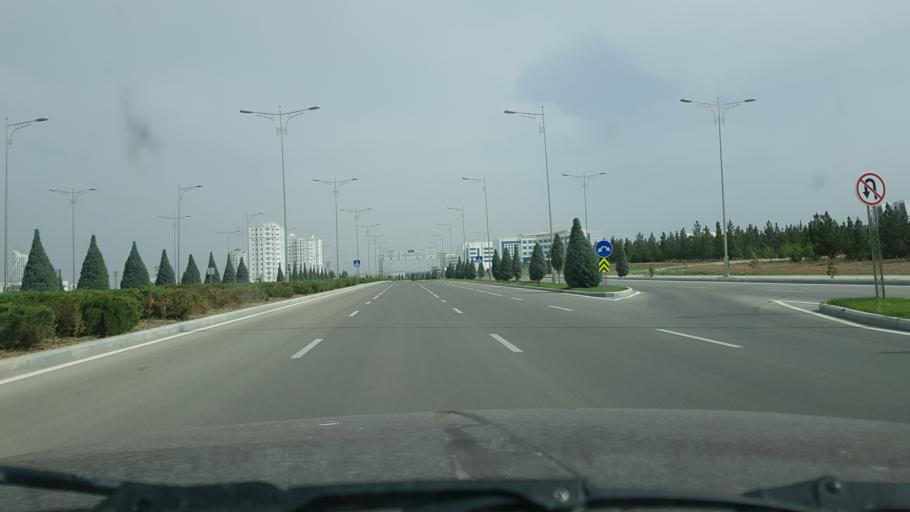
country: TM
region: Ahal
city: Ashgabat
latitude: 37.8812
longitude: 58.3500
